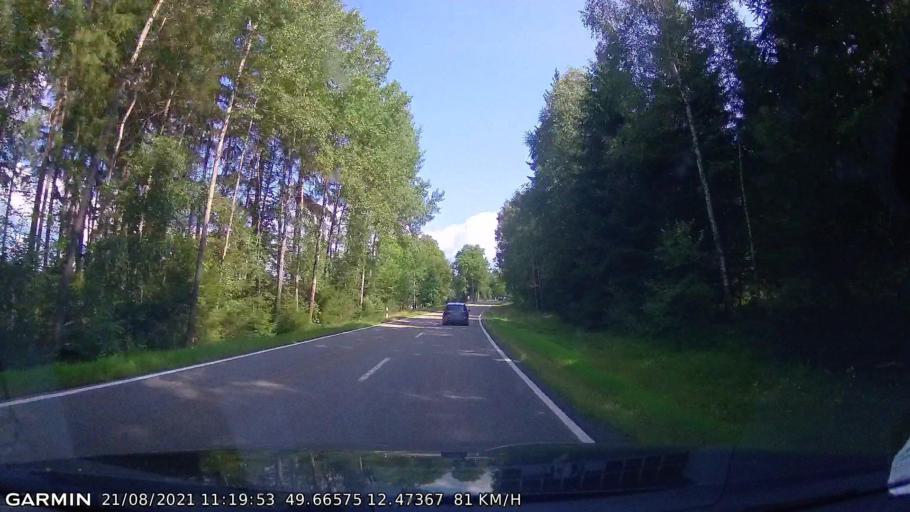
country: DE
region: Bavaria
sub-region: Upper Palatinate
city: Waidhaus
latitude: 49.6658
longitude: 12.4737
